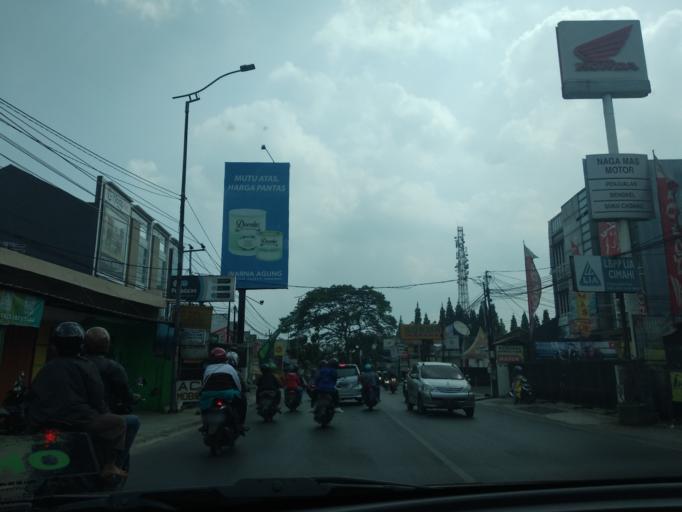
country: ID
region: West Java
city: Cimahi
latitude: -6.8690
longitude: 107.5323
